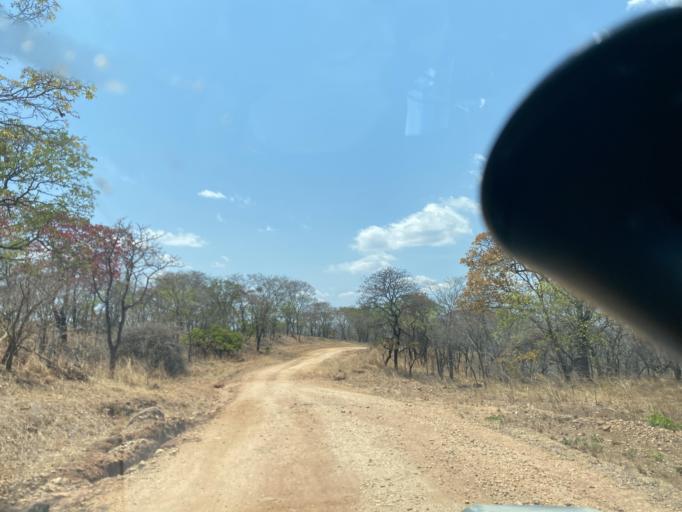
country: ZM
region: Lusaka
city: Luangwa
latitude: -15.0142
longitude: 29.7340
